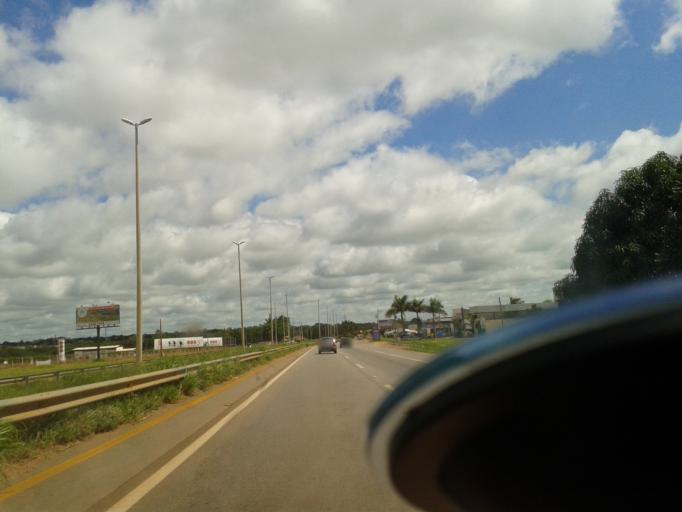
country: BR
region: Goias
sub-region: Goianira
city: Goianira
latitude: -16.5494
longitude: -49.4056
